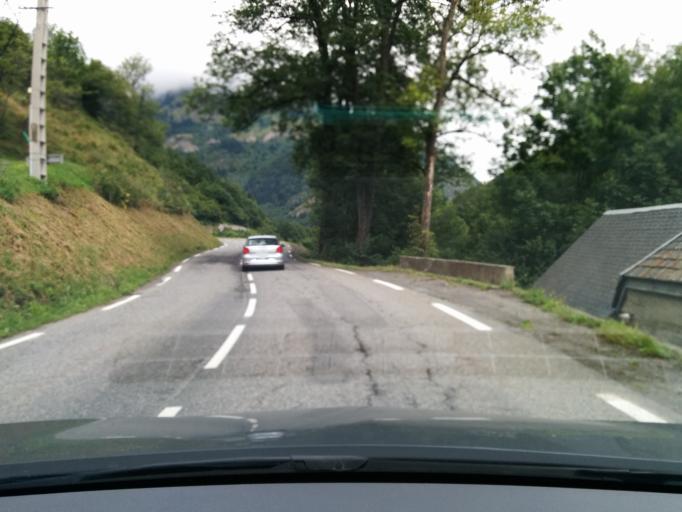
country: FR
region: Midi-Pyrenees
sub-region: Departement des Hautes-Pyrenees
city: Saint-Lary-Soulan
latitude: 42.7865
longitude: 0.2153
